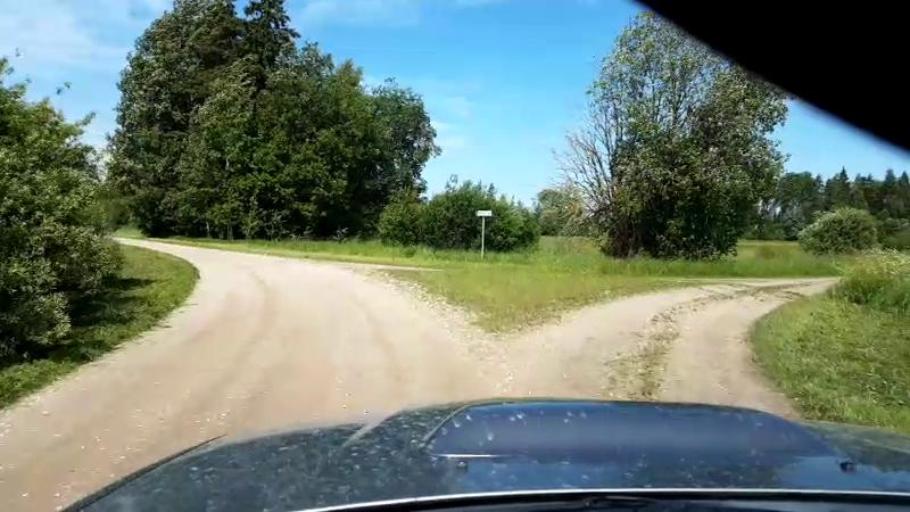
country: EE
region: Paernumaa
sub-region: Sindi linn
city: Sindi
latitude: 58.5176
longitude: 24.6612
